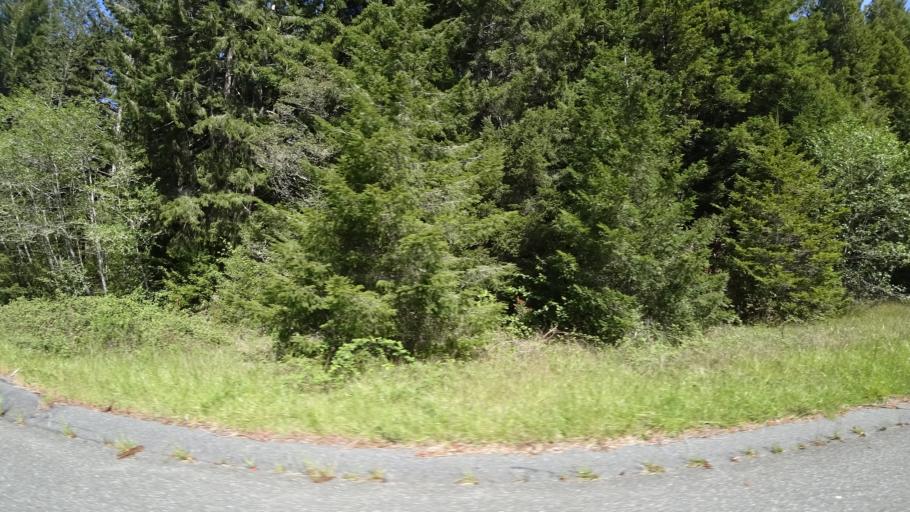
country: US
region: California
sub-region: Humboldt County
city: Westhaven-Moonstone
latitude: 41.3537
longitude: -124.0168
